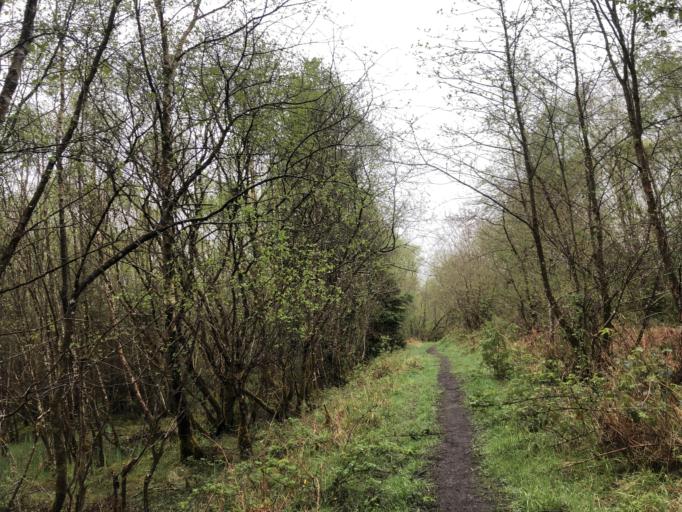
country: IE
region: Connaught
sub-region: County Leitrim
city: Carrick-on-Shannon
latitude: 53.9893
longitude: -8.1854
